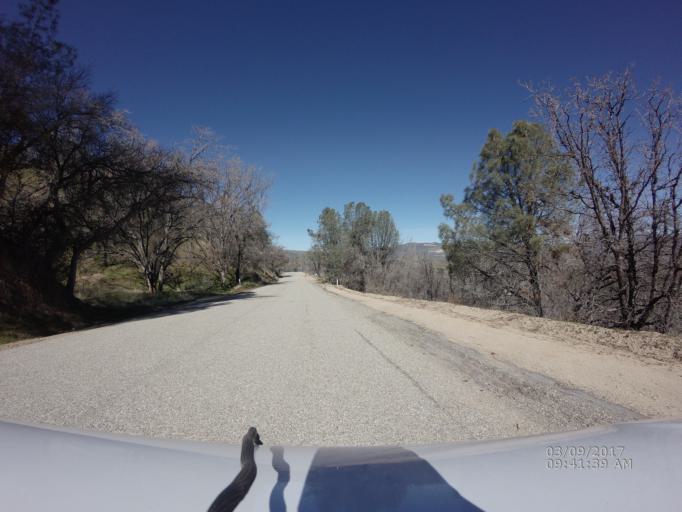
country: US
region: California
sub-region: Kern County
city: Lebec
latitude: 34.7579
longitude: -118.7190
